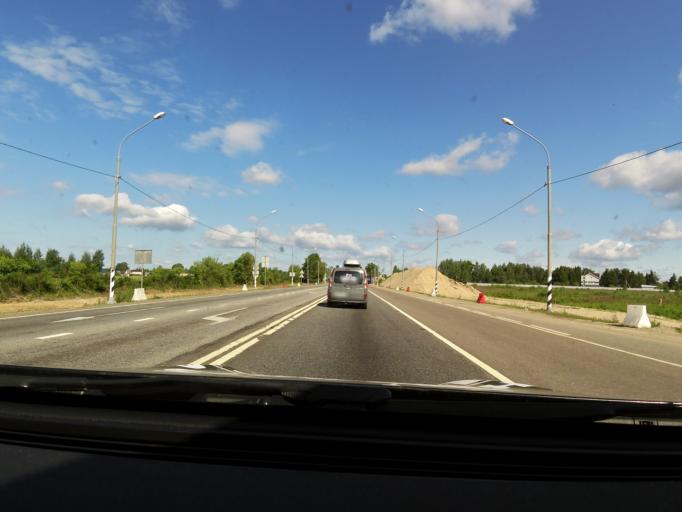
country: RU
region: Tverskaya
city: Tver
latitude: 56.8242
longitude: 35.8155
